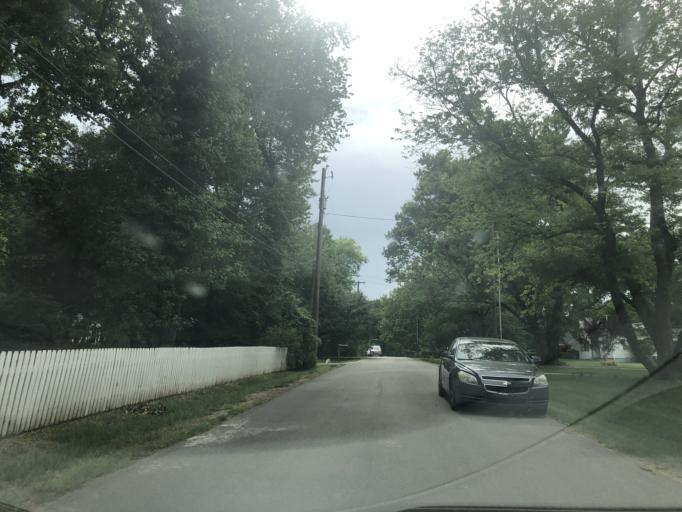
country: US
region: Tennessee
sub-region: Davidson County
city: Oak Hill
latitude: 36.0904
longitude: -86.7854
